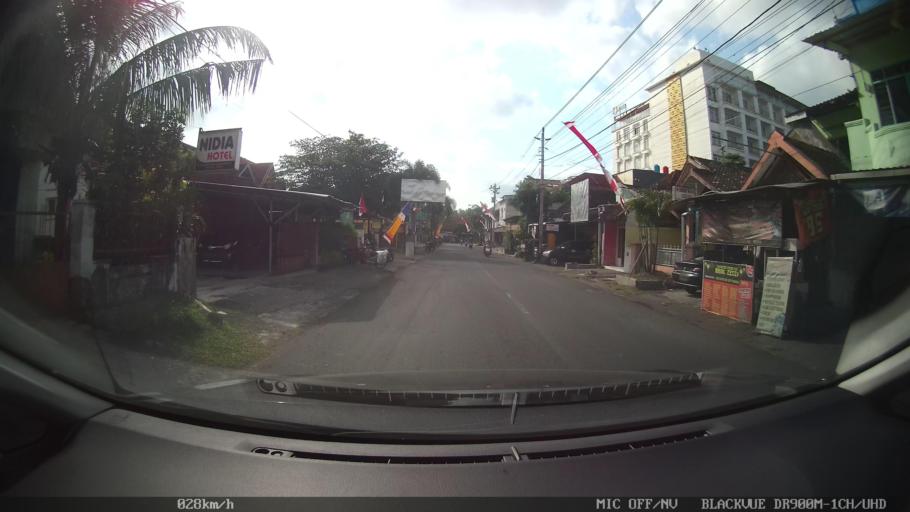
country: ID
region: Daerah Istimewa Yogyakarta
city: Kasihan
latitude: -7.8219
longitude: 110.3664
